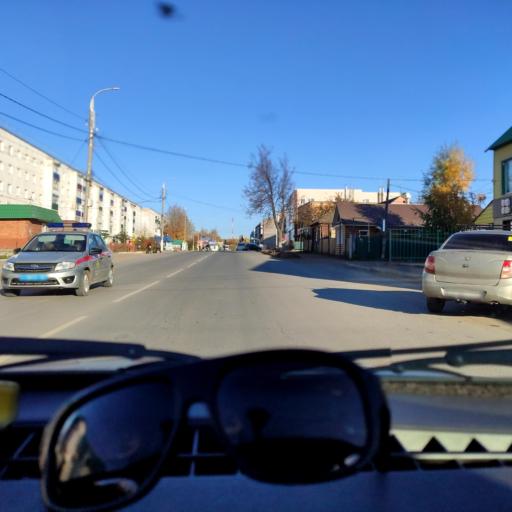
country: RU
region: Bashkortostan
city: Blagoveshchensk
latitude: 55.0472
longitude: 55.9574
